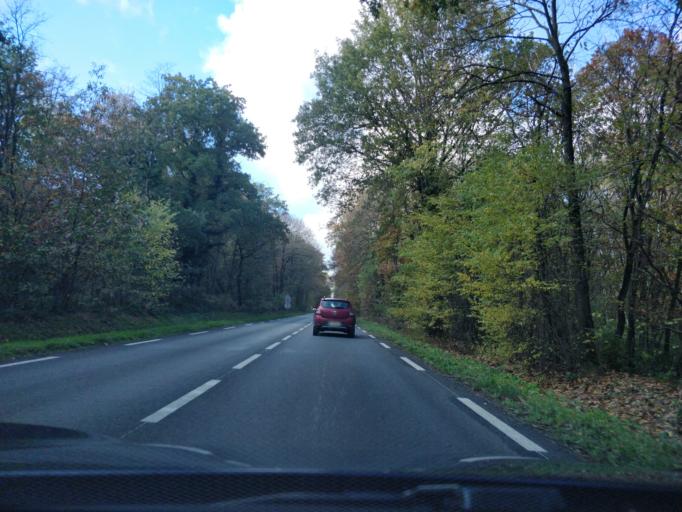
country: FR
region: Ile-de-France
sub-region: Departement de l'Essonne
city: Bruyeres-le-Chatel
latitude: 48.6072
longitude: 2.1926
